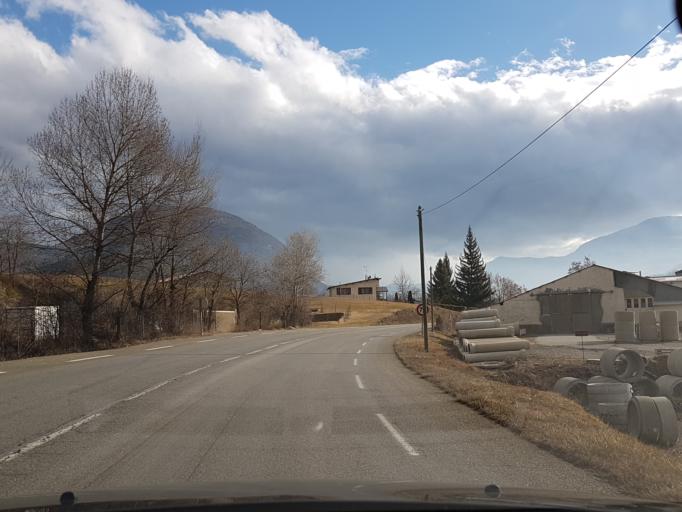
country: FR
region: Provence-Alpes-Cote d'Azur
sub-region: Departement des Hautes-Alpes
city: Tallard
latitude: 44.4800
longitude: 6.0912
